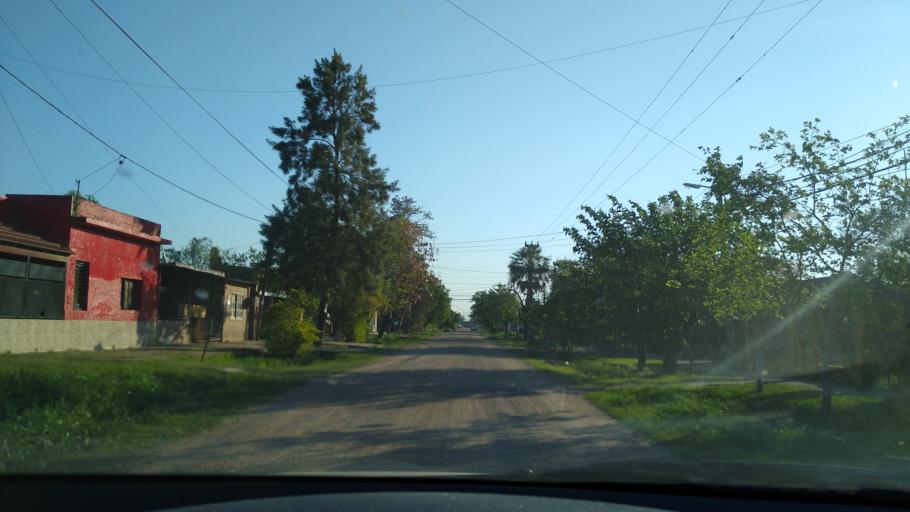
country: AR
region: Chaco
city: Barranqueras
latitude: -27.4910
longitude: -58.9327
